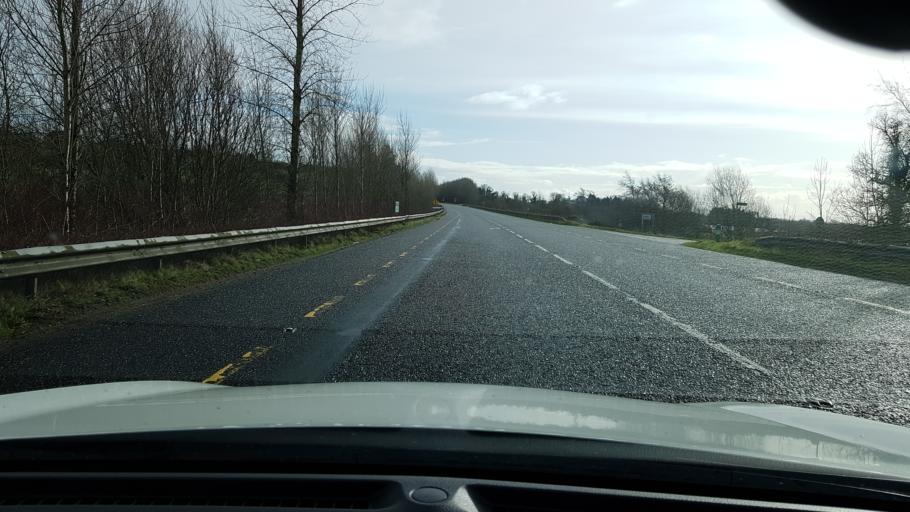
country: IE
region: Connaught
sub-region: County Leitrim
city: Carrick-on-Shannon
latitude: 53.9262
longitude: -7.9972
